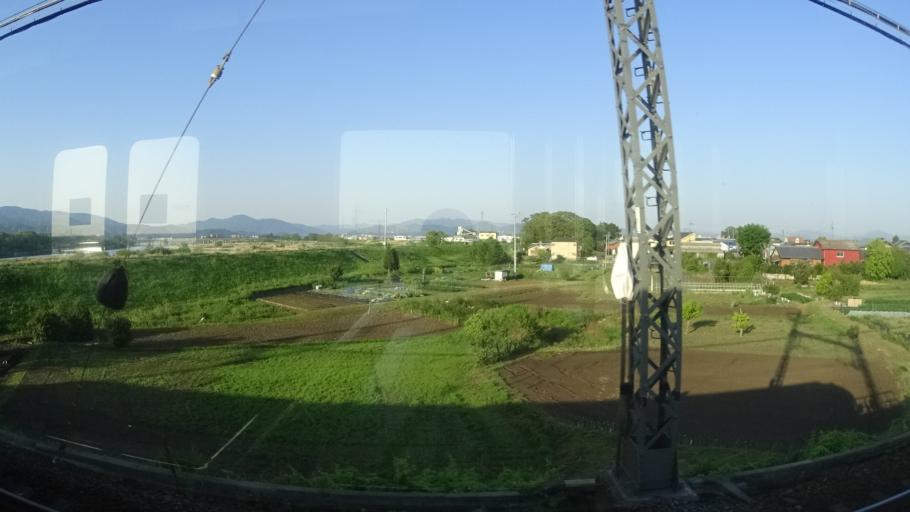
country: JP
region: Mie
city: Ise
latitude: 34.5111
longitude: 136.6871
